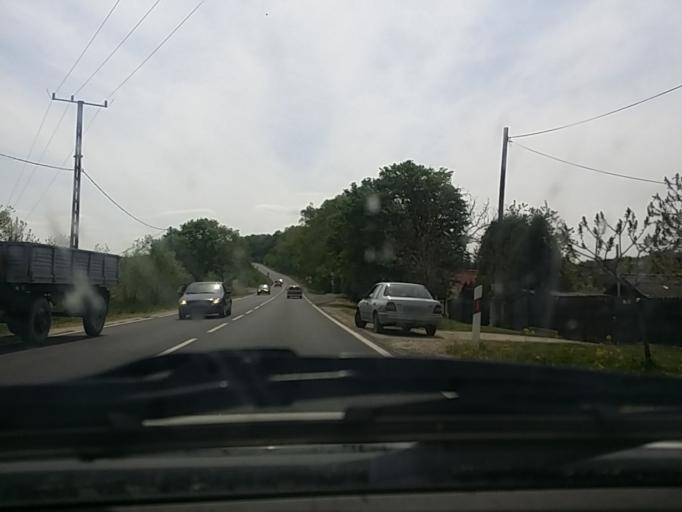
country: HU
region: Zala
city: Nagykanizsa
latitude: 46.4349
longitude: 17.0386
